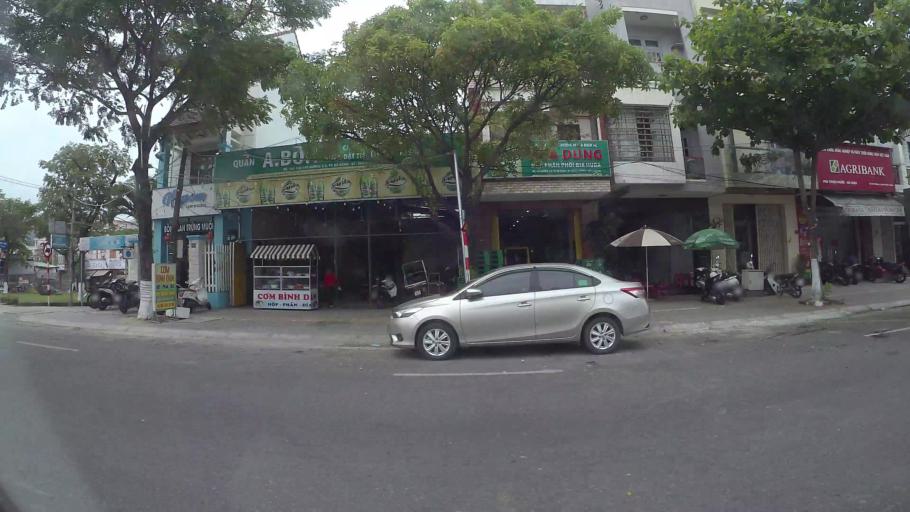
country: VN
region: Da Nang
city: Da Nang
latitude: 16.0867
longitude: 108.2164
